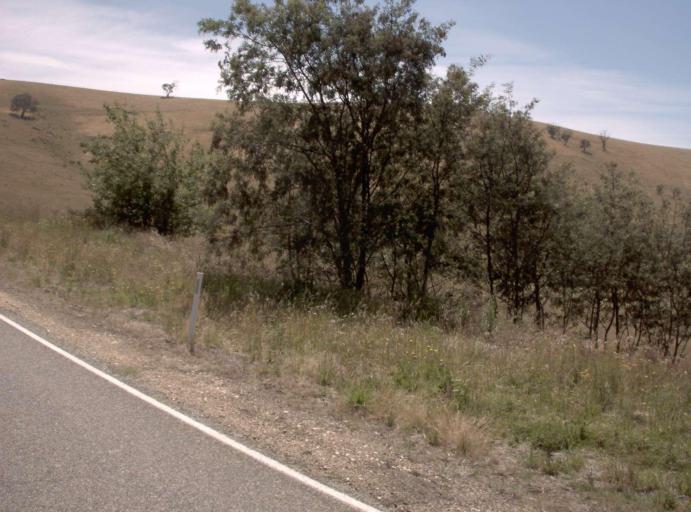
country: AU
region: Victoria
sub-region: Alpine
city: Mount Beauty
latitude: -37.0530
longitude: 147.6170
